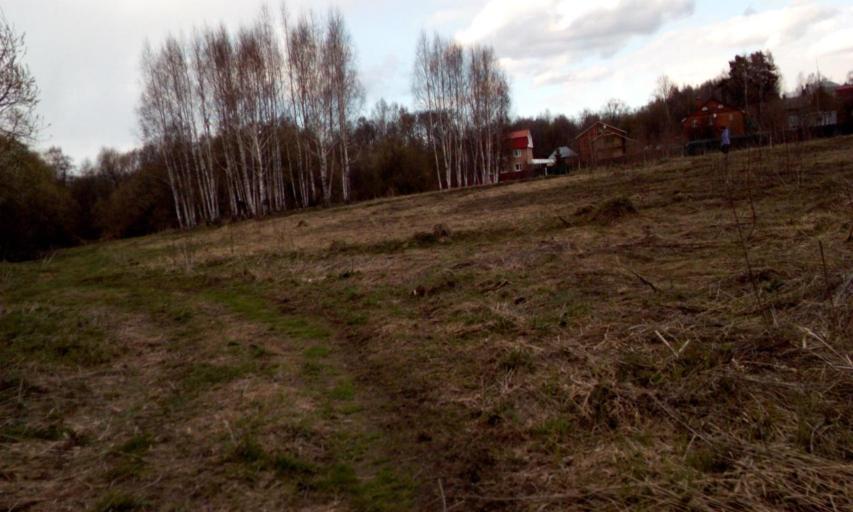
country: RU
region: Moskovskaya
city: Troitsk
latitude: 55.5154
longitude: 37.2637
